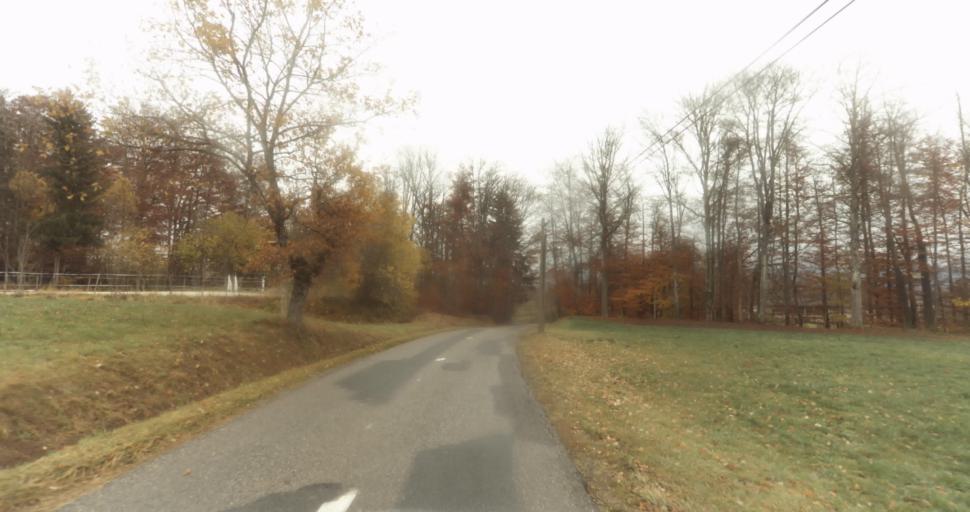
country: FR
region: Rhone-Alpes
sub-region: Departement de la Haute-Savoie
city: Evires
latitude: 46.0575
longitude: 6.2255
